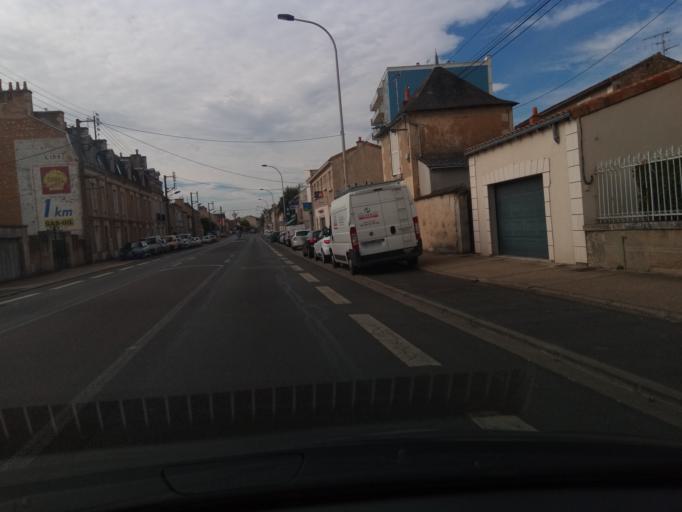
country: FR
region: Poitou-Charentes
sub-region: Departement de la Vienne
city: Biard
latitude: 46.5659
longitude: 0.3187
